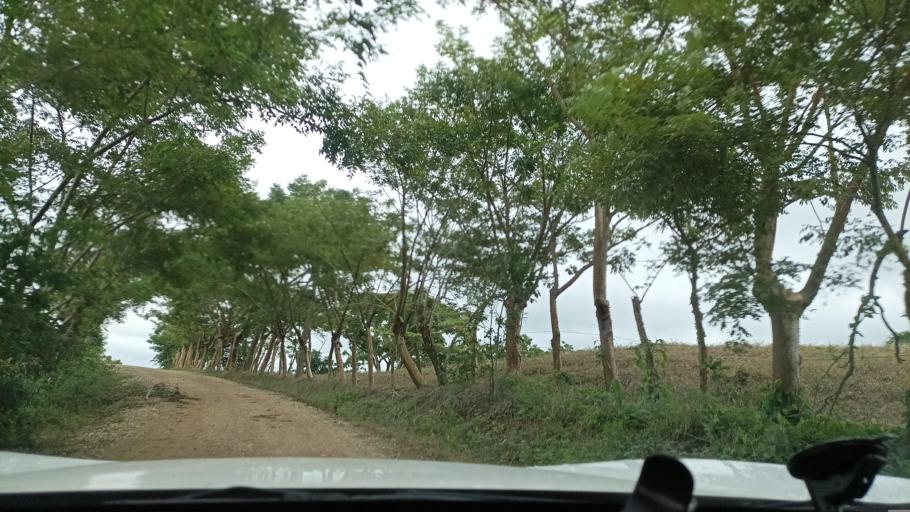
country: MX
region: Veracruz
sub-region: Moloacan
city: Cuichapa
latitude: 17.7884
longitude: -94.3598
